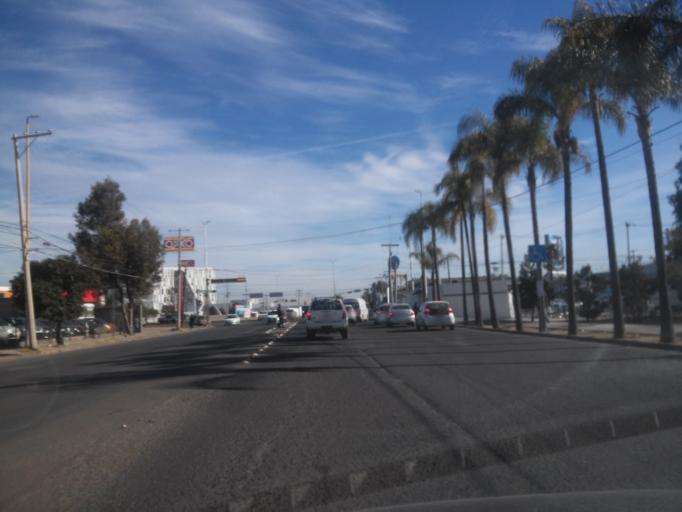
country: MX
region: Durango
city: Victoria de Durango
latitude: 24.0420
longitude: -104.6590
